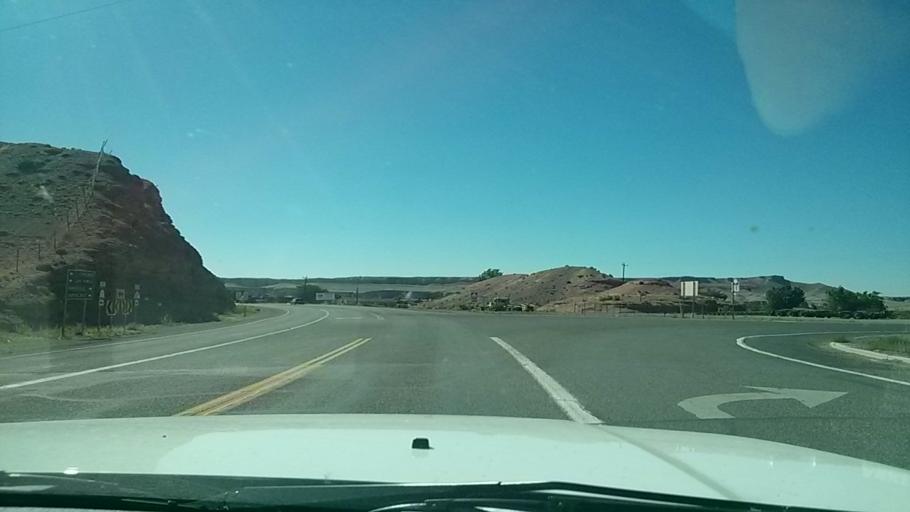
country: US
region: Utah
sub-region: Emery County
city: Ferron
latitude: 38.3730
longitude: -110.7045
